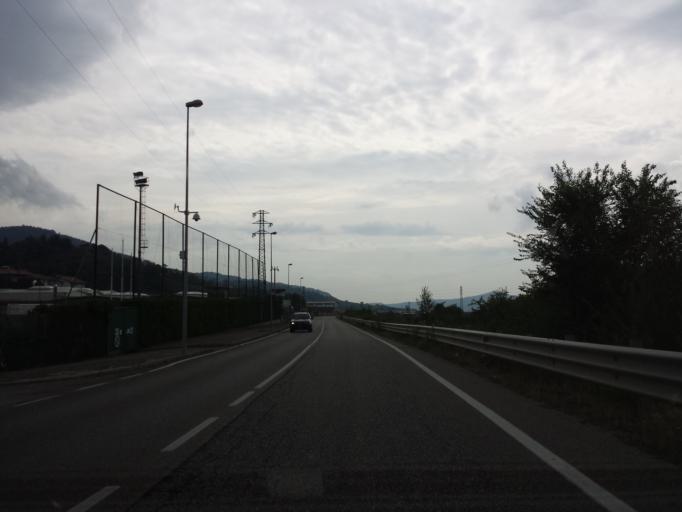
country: IT
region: Veneto
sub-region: Provincia di Verona
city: San Giovanni Ilarione
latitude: 45.5170
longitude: 11.2362
